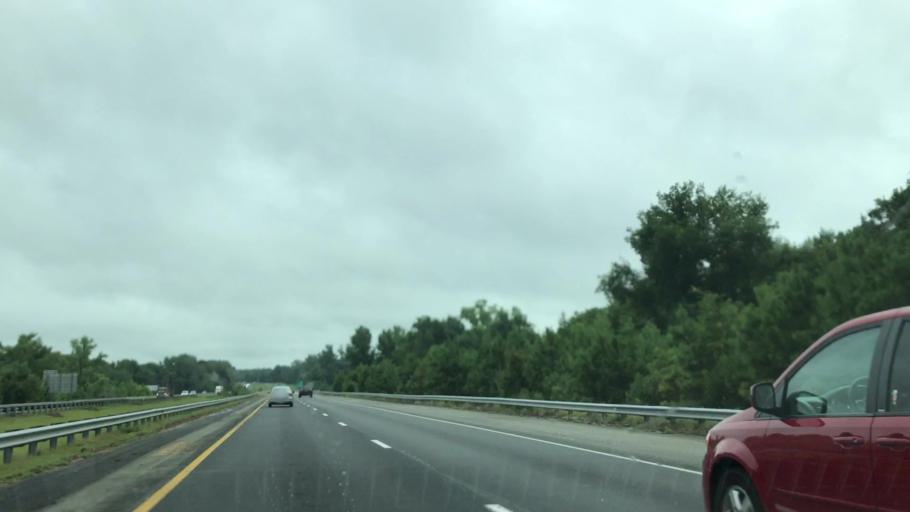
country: US
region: North Carolina
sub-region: Halifax County
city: Weldon
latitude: 36.4474
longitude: -77.6230
